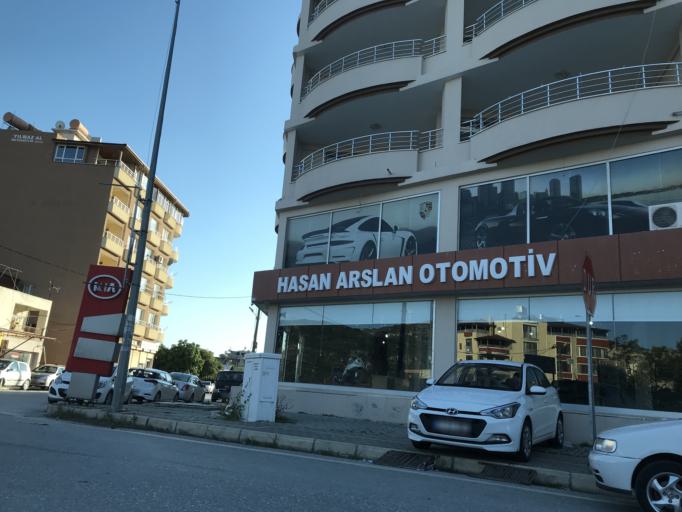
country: TR
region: Hatay
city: Samandag
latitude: 36.0799
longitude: 35.9917
